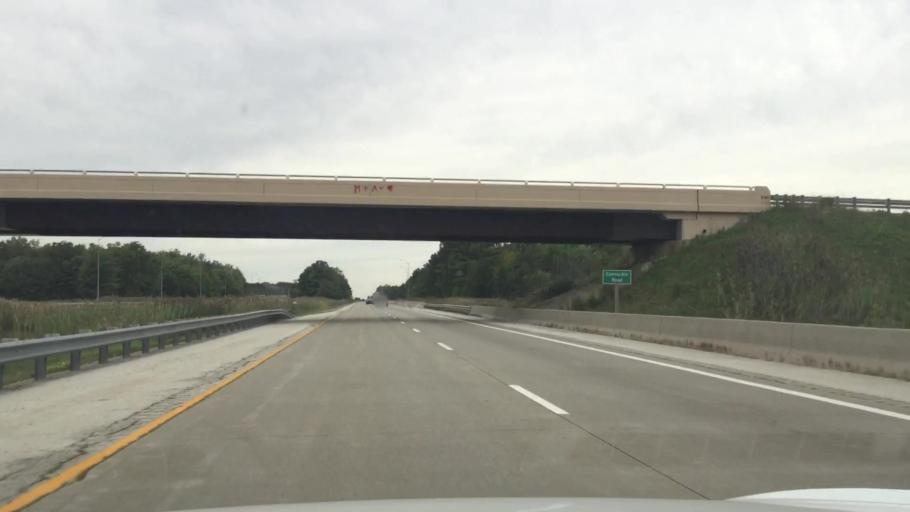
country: CA
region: Ontario
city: Camlachie
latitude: 42.9923
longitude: -82.1630
